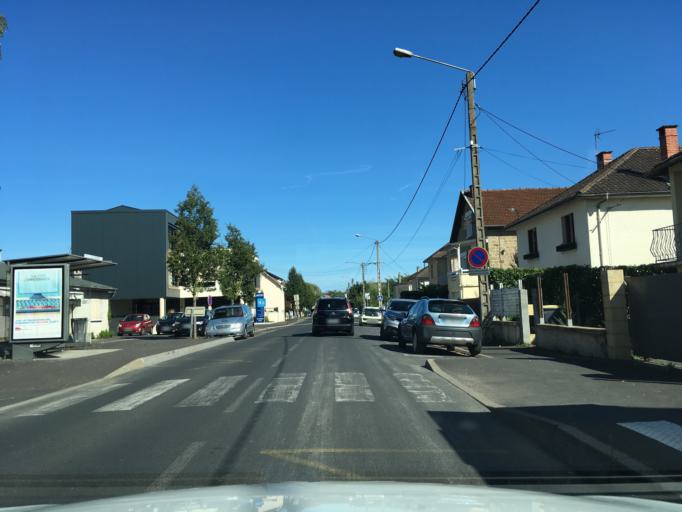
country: FR
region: Limousin
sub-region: Departement de la Correze
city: Brive-la-Gaillarde
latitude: 45.1602
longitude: 1.5002
